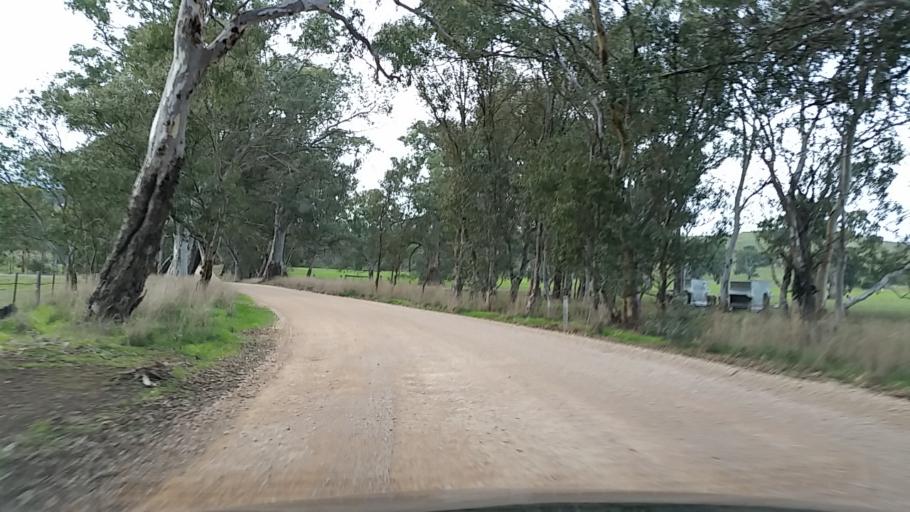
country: AU
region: South Australia
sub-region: Adelaide Hills
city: Birdwood
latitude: -34.9189
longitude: 139.0198
